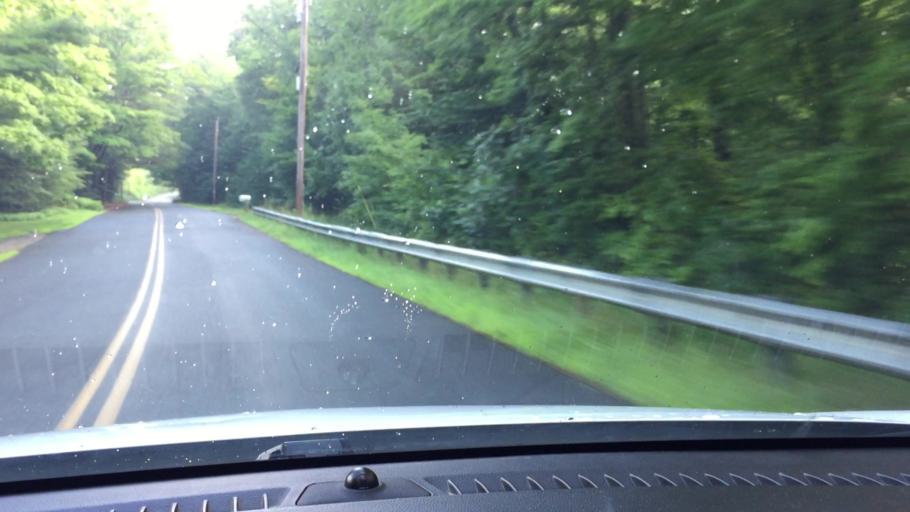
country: US
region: Massachusetts
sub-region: Berkshire County
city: Becket
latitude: 42.4030
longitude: -72.9790
